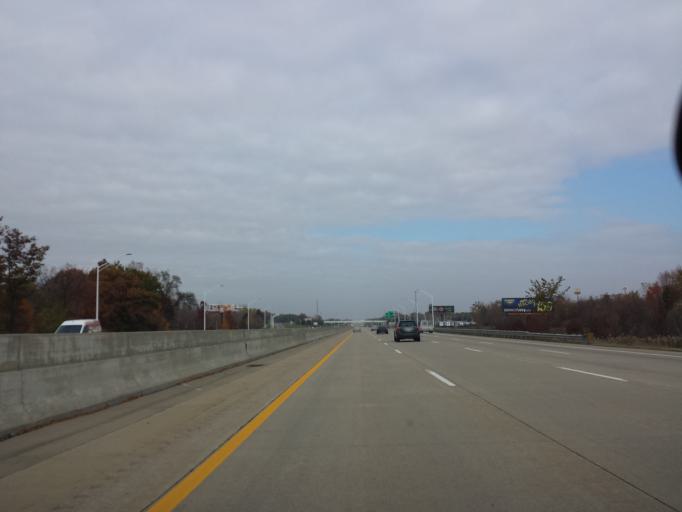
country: US
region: Michigan
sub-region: Genesee County
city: Clio
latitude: 43.1702
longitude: -83.7686
